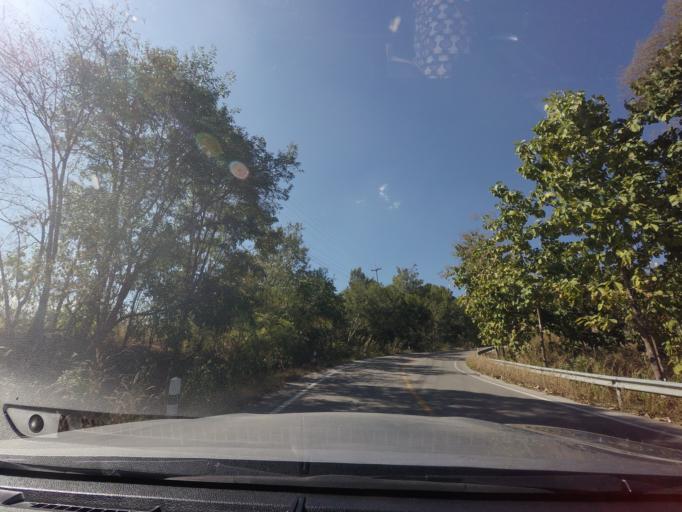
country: TH
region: Lampang
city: Chae Hom
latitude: 18.6208
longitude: 99.6221
